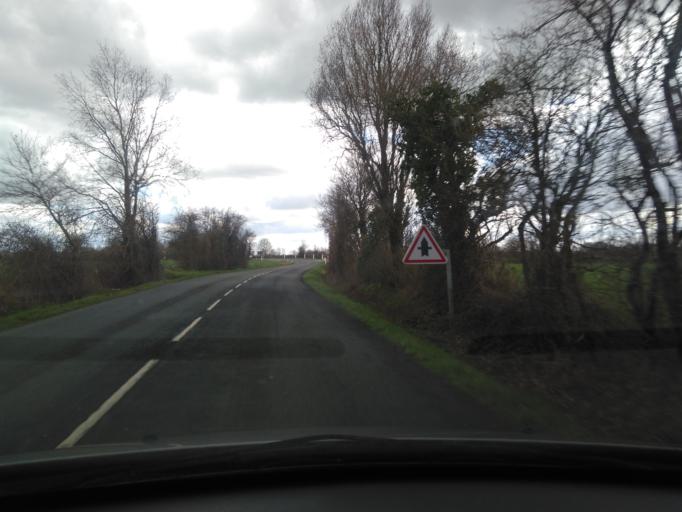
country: FR
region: Pays de la Loire
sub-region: Departement de la Vendee
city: Les Essarts
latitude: 46.7513
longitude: -1.2134
